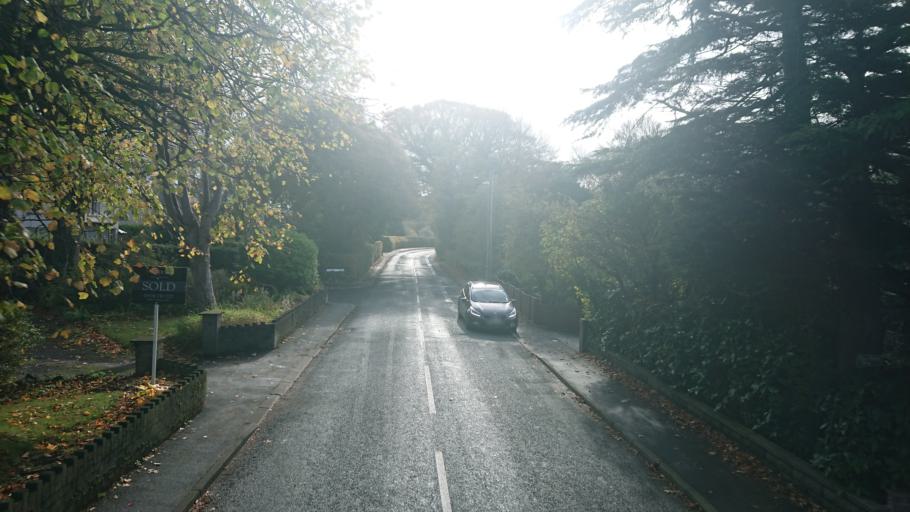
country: GB
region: England
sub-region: Lancashire
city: Bolton le Sands
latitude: 54.0873
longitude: -2.8097
